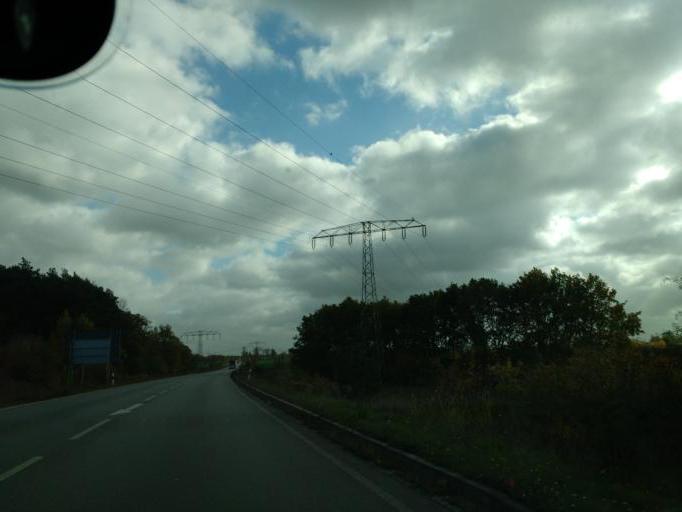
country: DE
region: Brandenburg
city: Neuenhagen
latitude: 52.5509
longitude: 13.6974
